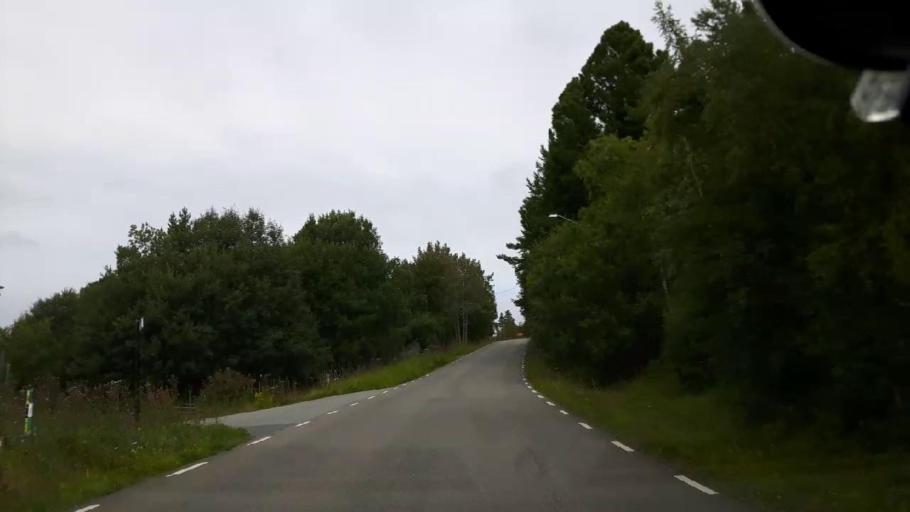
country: SE
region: Jaemtland
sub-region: OEstersunds Kommun
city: Ostersund
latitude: 63.1723
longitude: 14.5173
